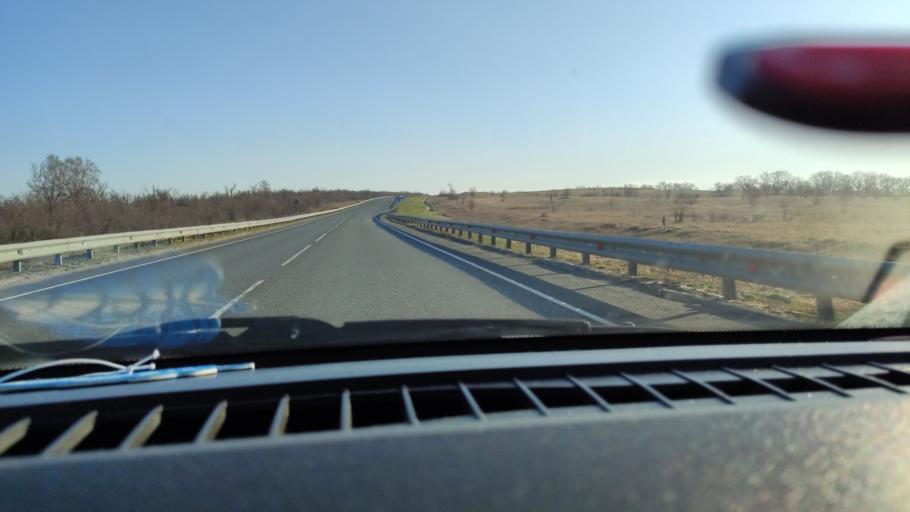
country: RU
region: Saratov
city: Balakovo
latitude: 52.1991
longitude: 47.8630
